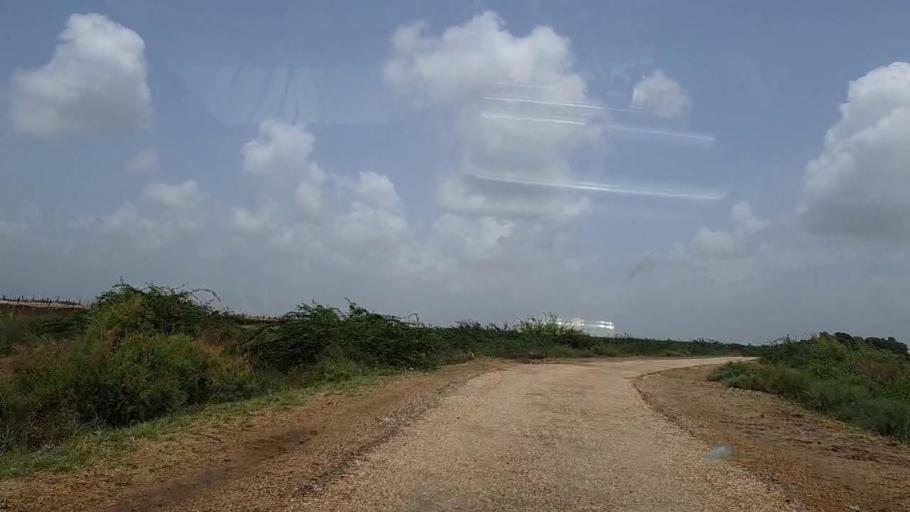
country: PK
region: Sindh
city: Keti Bandar
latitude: 24.1689
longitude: 67.5418
